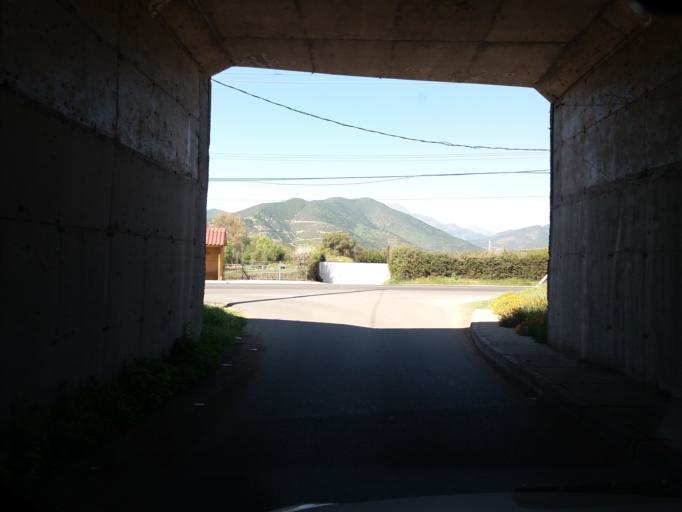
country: CL
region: Valparaiso
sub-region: Provincia de Quillota
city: Quillota
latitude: -32.9453
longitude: -71.2859
